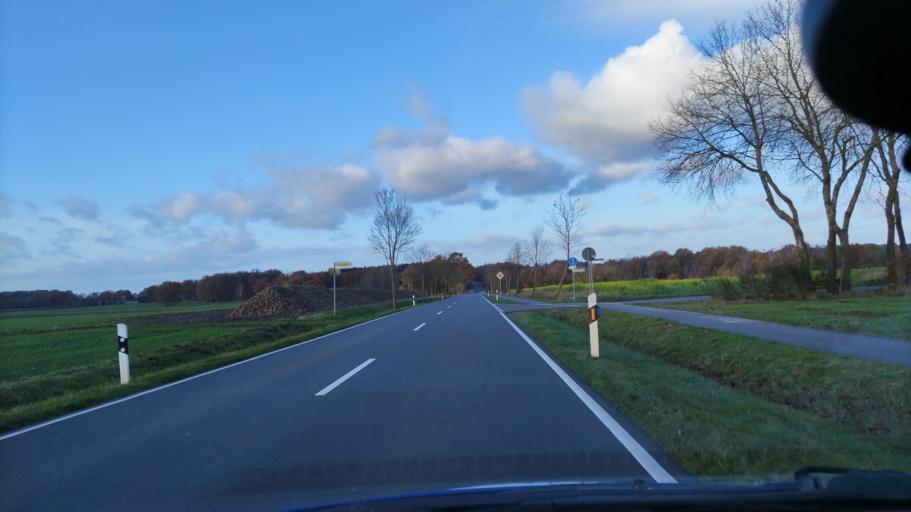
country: DE
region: Lower Saxony
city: Schneverdingen
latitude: 53.0655
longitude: 9.8166
